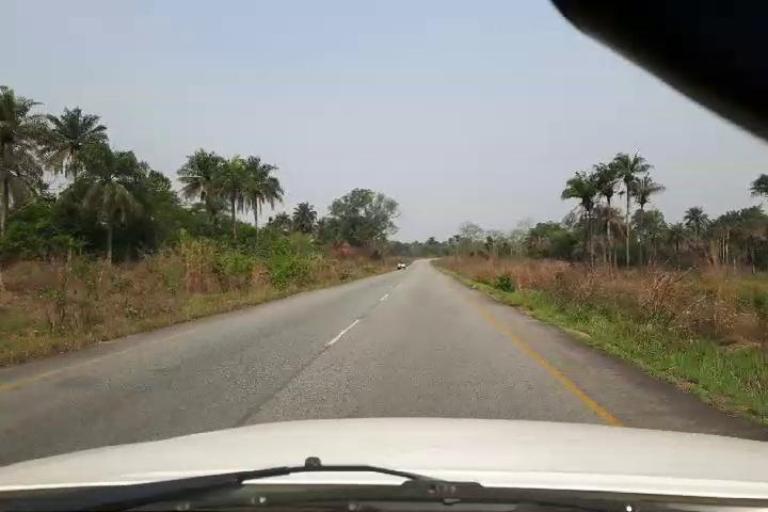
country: SL
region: Southern Province
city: Largo
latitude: 8.3062
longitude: -12.2054
